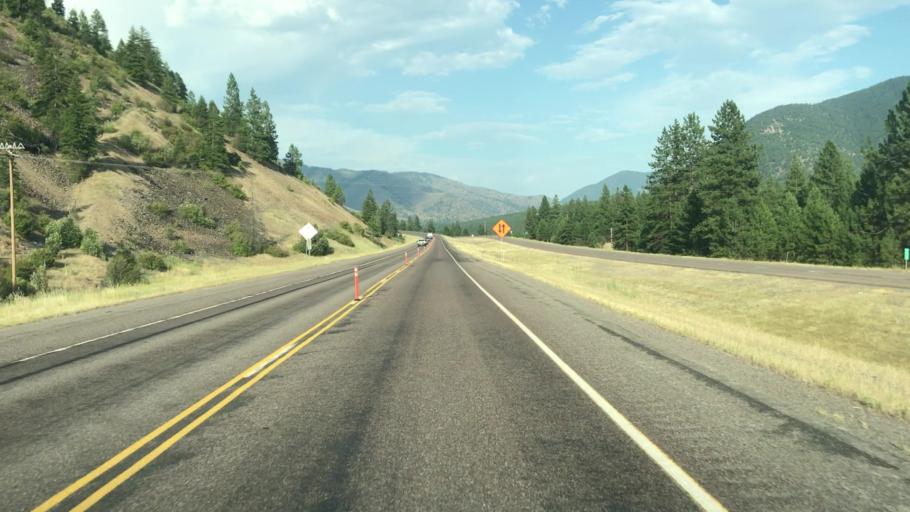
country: US
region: Montana
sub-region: Mineral County
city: Superior
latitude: 47.0127
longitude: -114.7053
